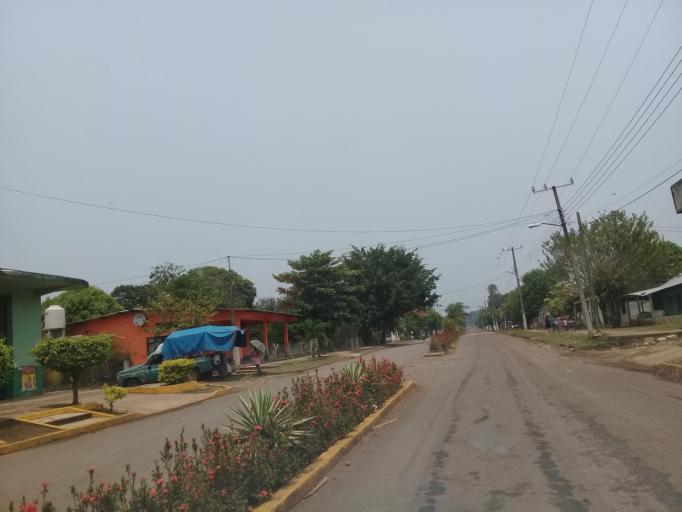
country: MX
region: Veracruz
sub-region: Tezonapa
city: Laguna Chica (Pueblo Nuevo)
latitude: 18.5161
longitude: -96.7190
